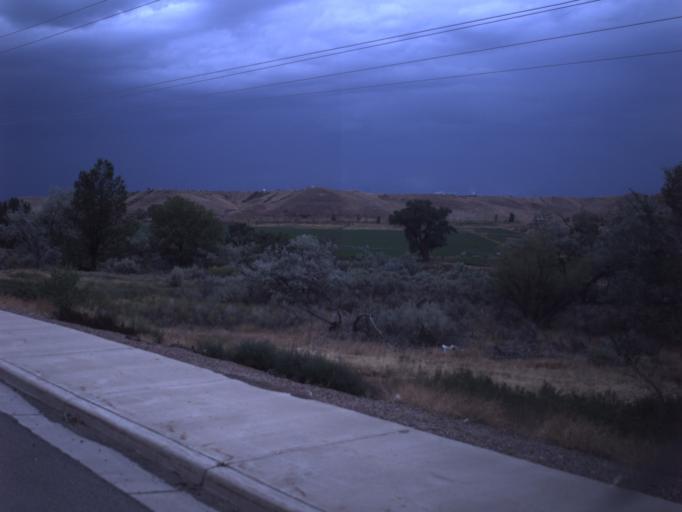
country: US
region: Utah
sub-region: Duchesne County
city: Roosevelt
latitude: 40.3072
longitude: -110.0053
